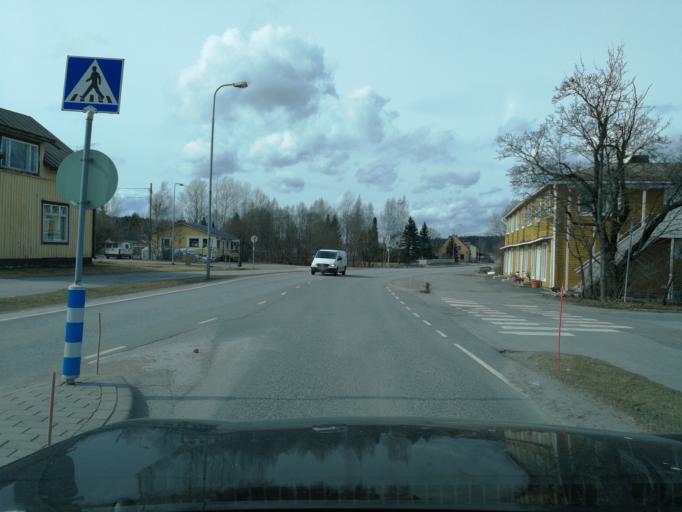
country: FI
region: Uusimaa
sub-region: Helsinki
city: Siuntio
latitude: 60.1421
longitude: 24.2241
